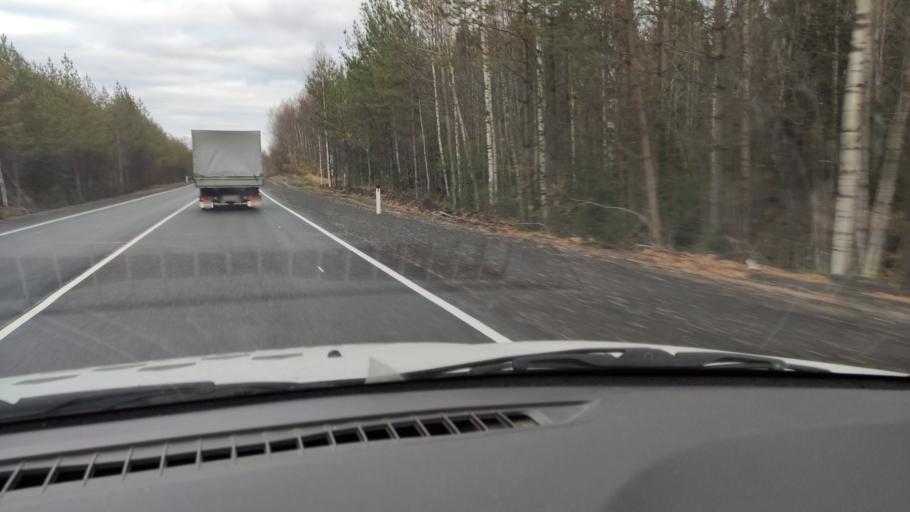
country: RU
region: Kirov
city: Chernaya Kholunitsa
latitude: 58.8736
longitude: 51.5077
